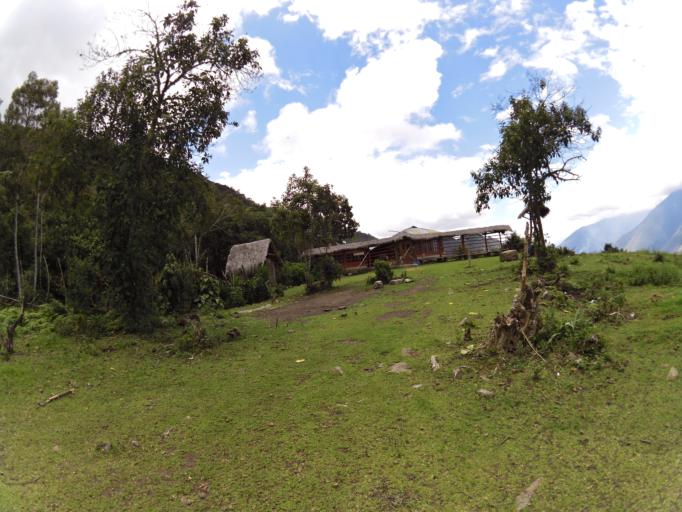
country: PE
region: Cusco
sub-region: Provincia de La Convencion
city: Santa Teresa
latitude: -13.1858
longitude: -72.5814
